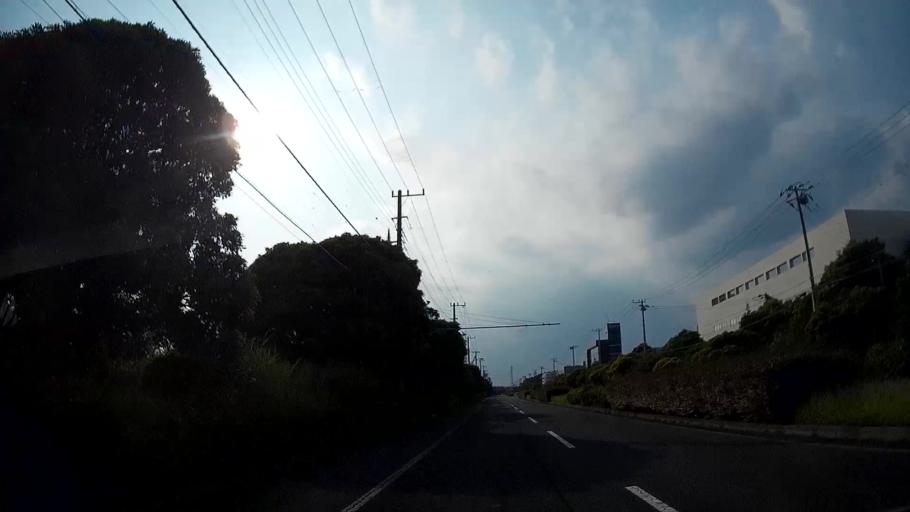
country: JP
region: Chiba
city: Funabashi
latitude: 35.6568
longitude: 140.0193
